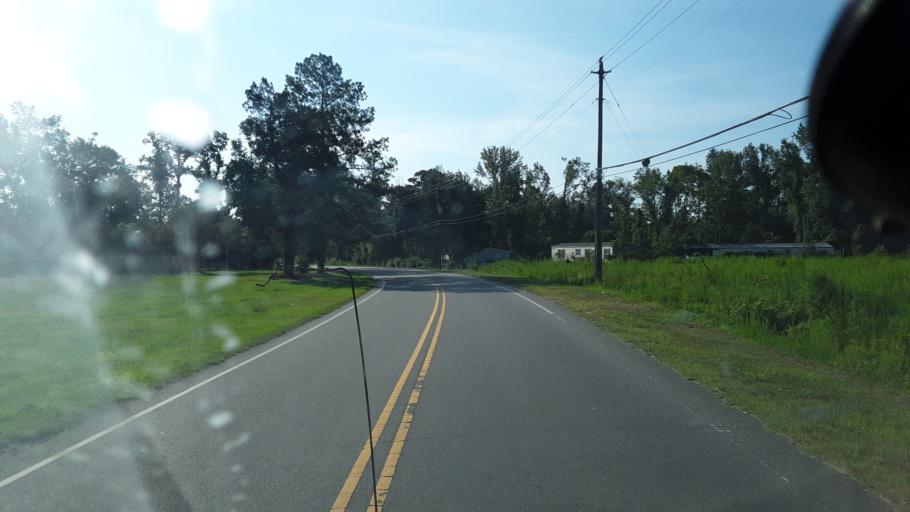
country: US
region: North Carolina
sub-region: Brunswick County
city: Leland
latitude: 34.2512
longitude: -78.0366
